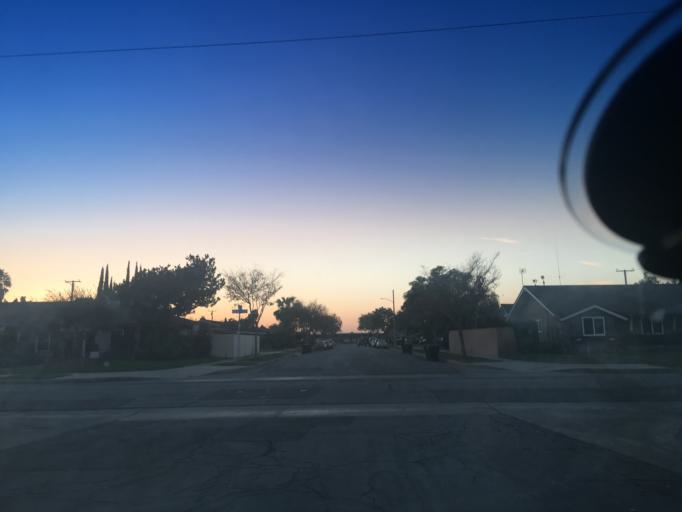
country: US
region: California
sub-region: Orange County
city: Anaheim
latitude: 33.8220
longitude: -117.8778
